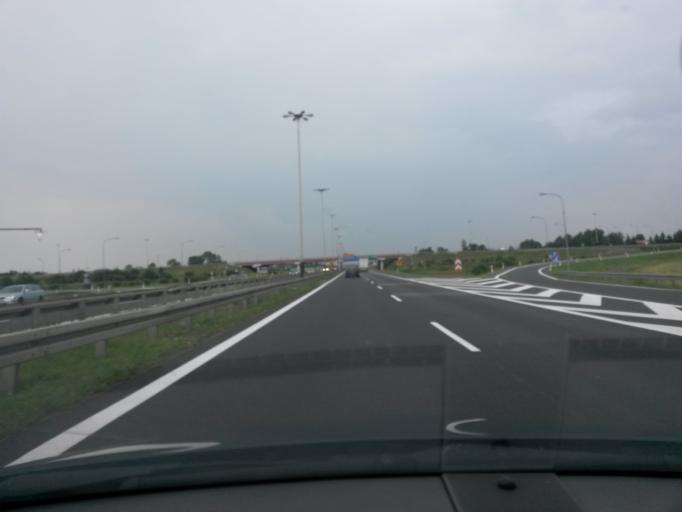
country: PL
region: Lodz Voivodeship
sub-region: Piotrkow Trybunalski
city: Piotrkow Trybunalski
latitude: 51.4073
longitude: 19.6340
